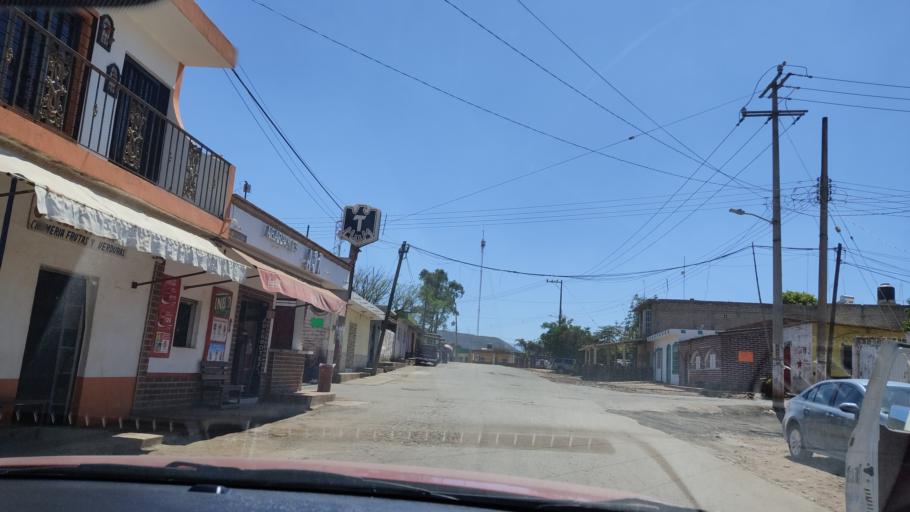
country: MX
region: Nayarit
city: Santa Maria del Oro
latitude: 21.4237
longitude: -104.6100
